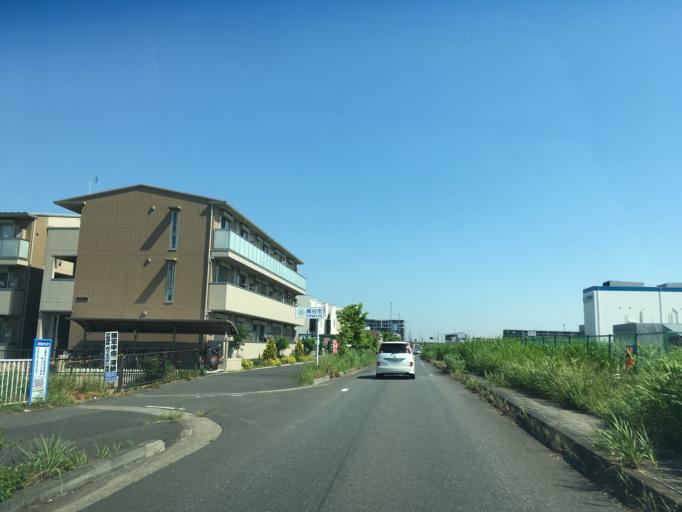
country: JP
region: Saitama
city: Yoshikawa
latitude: 35.8707
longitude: 139.8277
